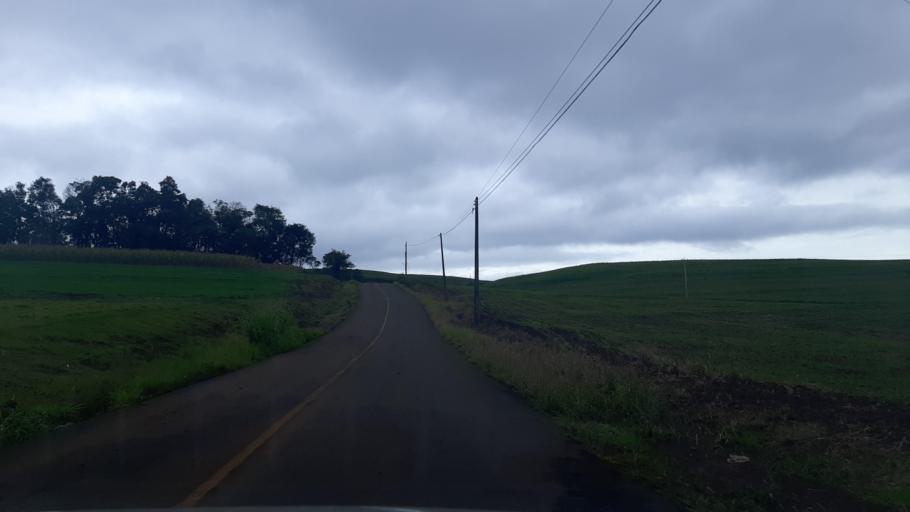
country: BR
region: Parana
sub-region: Ampere
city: Ampere
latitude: -26.0399
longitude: -53.4917
